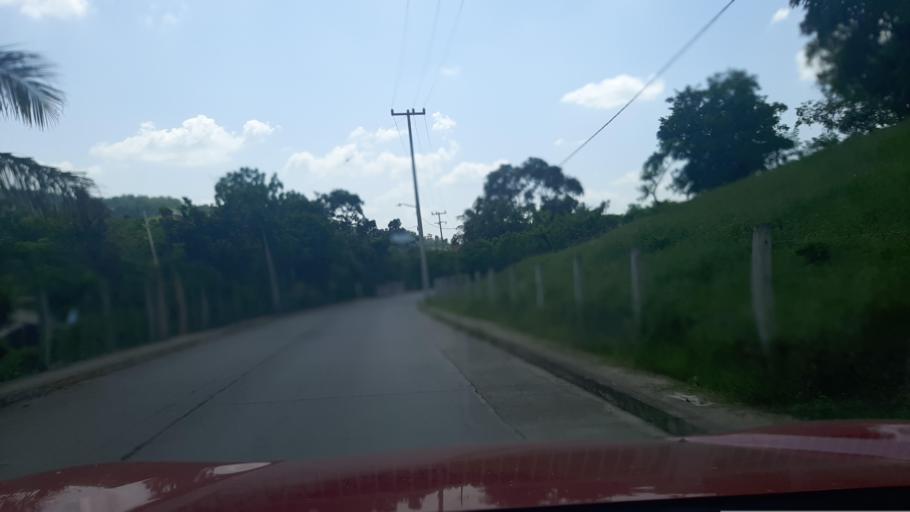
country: MX
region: Veracruz
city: Coatzintla
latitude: 20.4976
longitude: -97.4335
